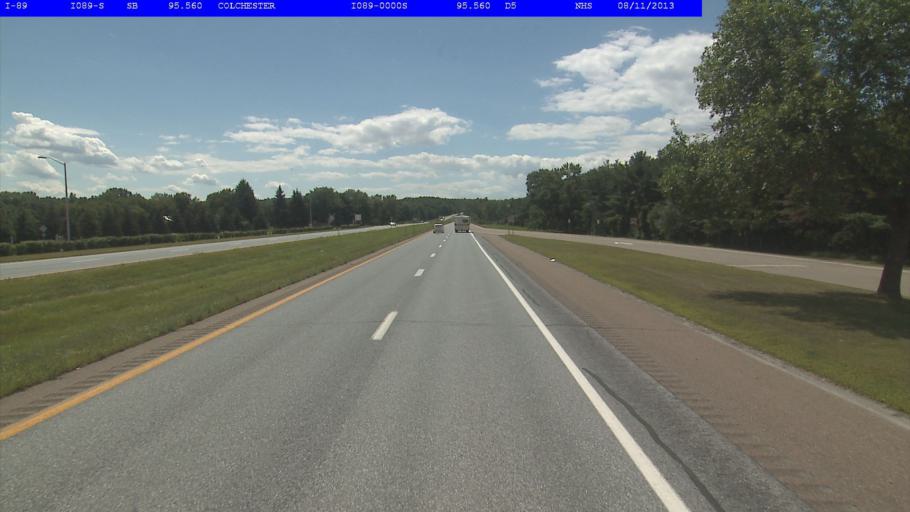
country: US
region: Vermont
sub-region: Chittenden County
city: Colchester
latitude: 44.5578
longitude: -73.1826
